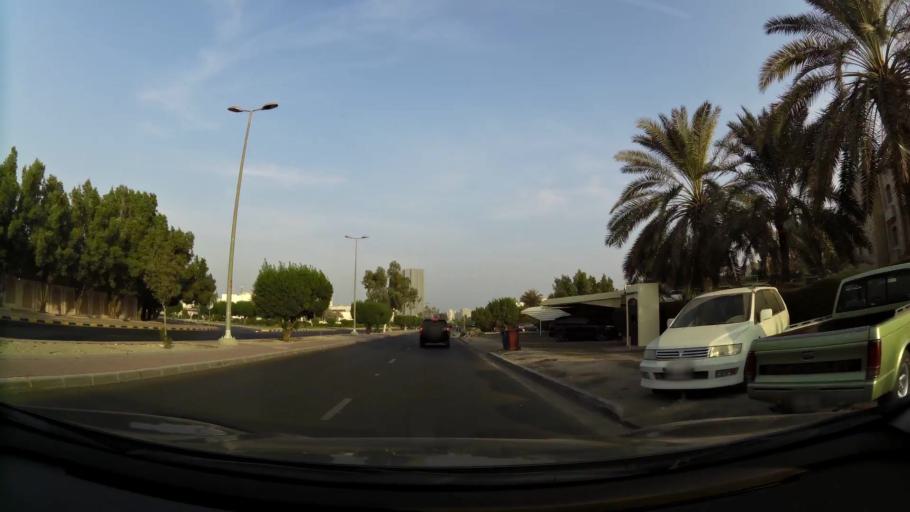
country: KW
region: Mubarak al Kabir
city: Sabah as Salim
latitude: 29.2577
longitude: 48.0725
